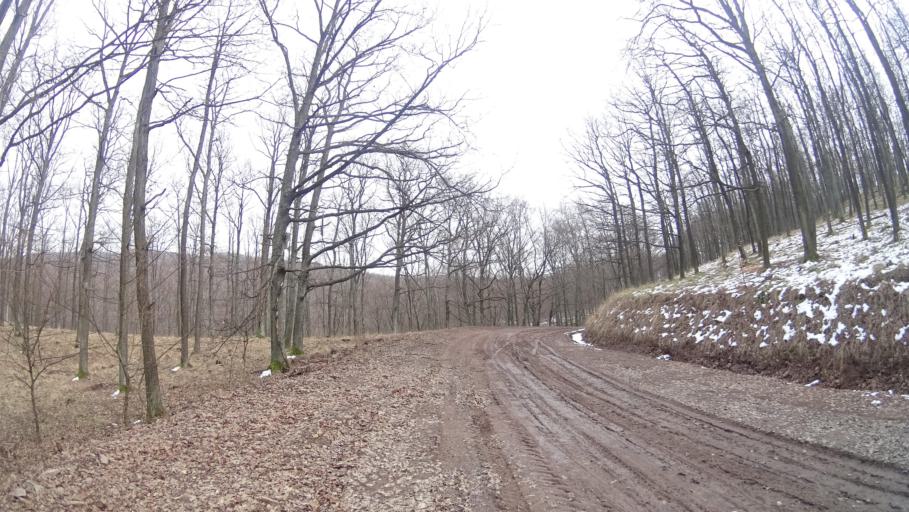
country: HU
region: Pest
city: Szob
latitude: 47.9069
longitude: 18.8966
